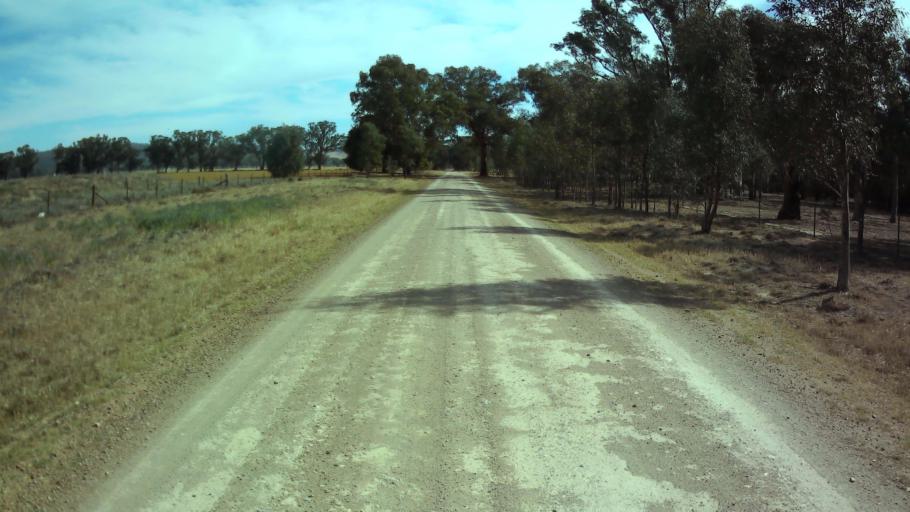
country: AU
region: New South Wales
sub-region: Weddin
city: Grenfell
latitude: -33.7031
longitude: 148.3018
